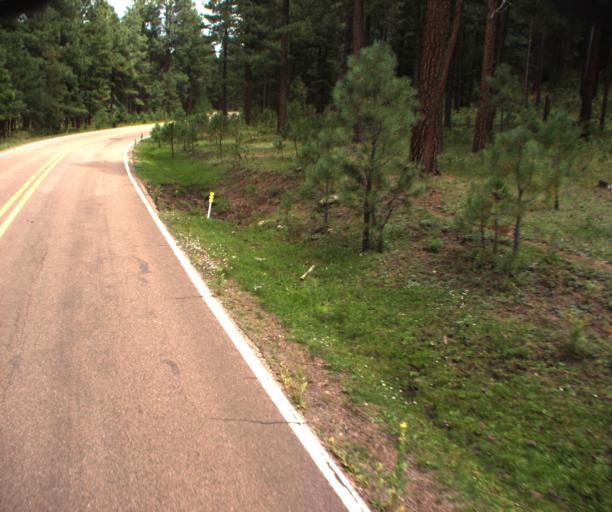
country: US
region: Arizona
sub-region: Navajo County
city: Pinetop-Lakeside
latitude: 34.0432
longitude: -109.7413
